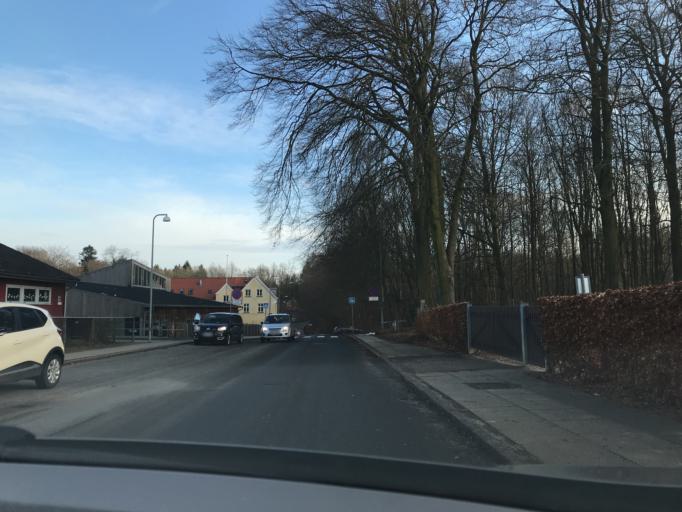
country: DK
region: South Denmark
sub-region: Vejle Kommune
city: Vejle
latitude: 55.6930
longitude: 9.5278
